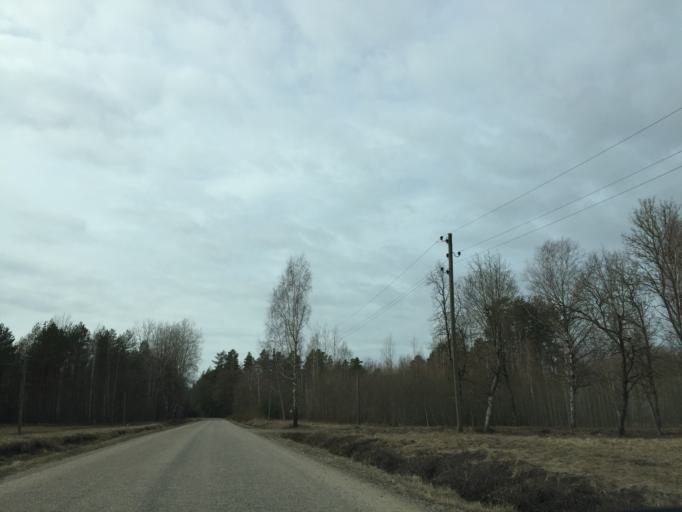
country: LV
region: Garkalne
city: Garkalne
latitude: 57.0747
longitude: 24.4416
